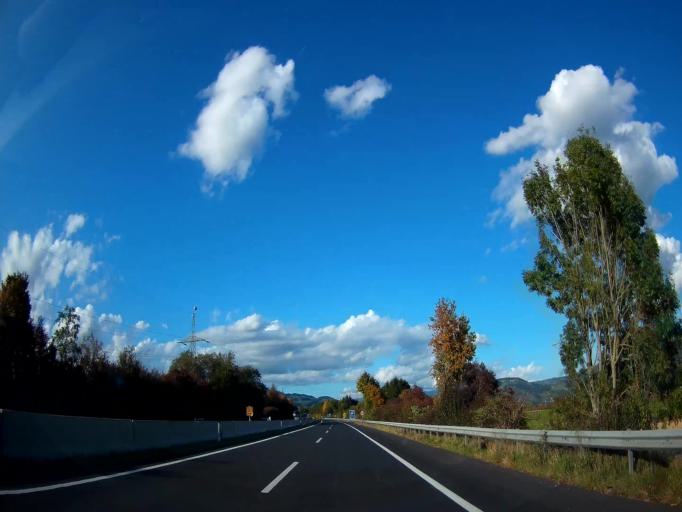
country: AT
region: Carinthia
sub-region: Politischer Bezirk Wolfsberg
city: Wolfsberg
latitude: 46.8150
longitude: 14.8229
